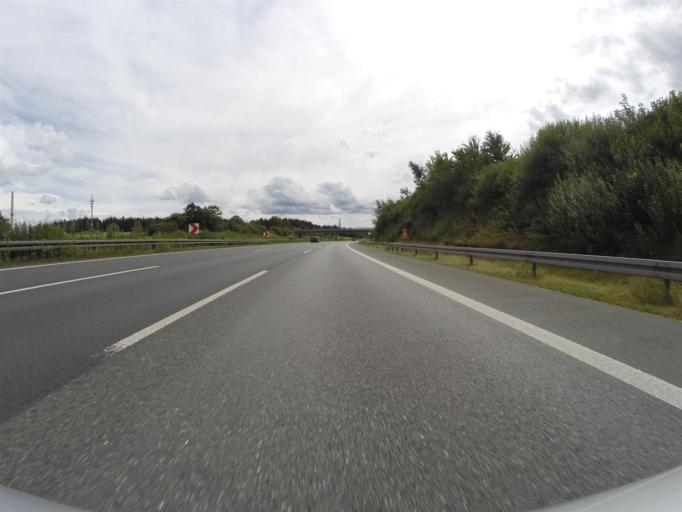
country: DE
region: Bavaria
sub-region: Upper Franconia
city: Munchberg
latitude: 50.1536
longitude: 11.7492
